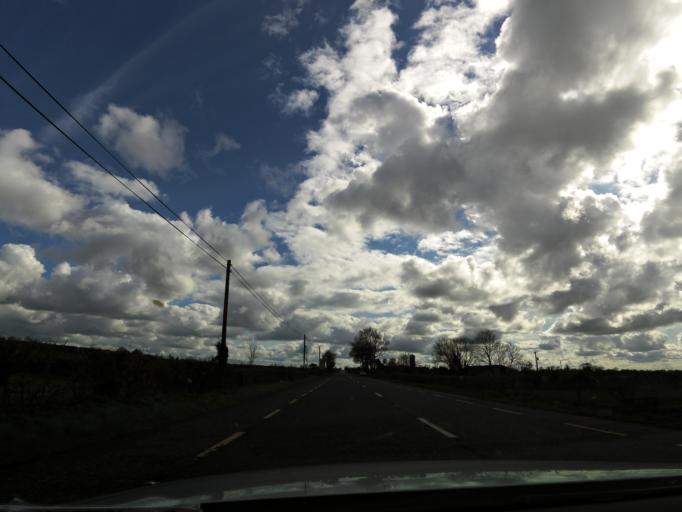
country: IE
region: Leinster
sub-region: Laois
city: Rathdowney
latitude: 52.7655
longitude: -7.5437
